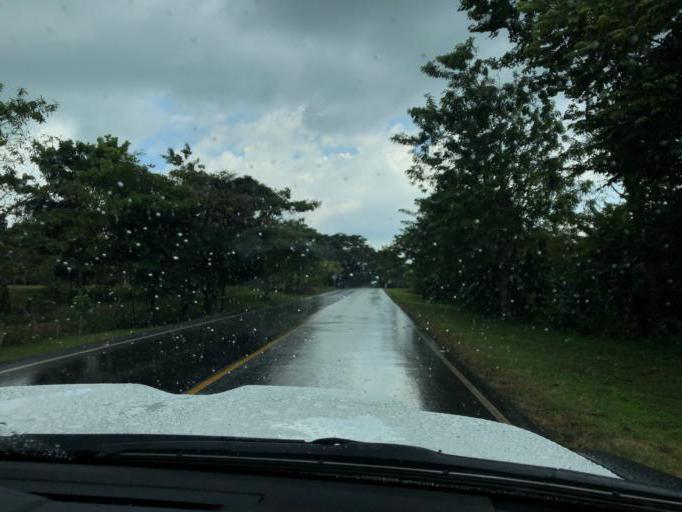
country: NI
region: Chontales
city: Villa Sandino
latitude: 12.0210
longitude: -84.9529
